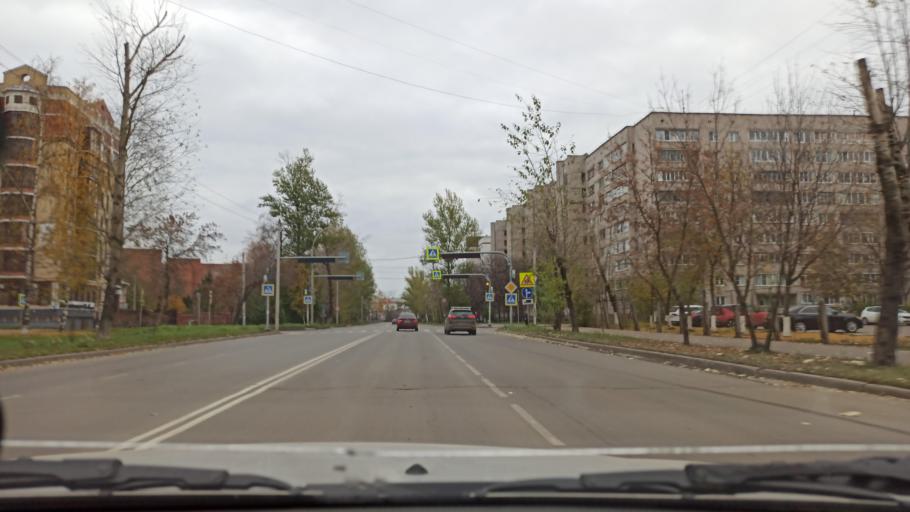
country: RU
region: Vologda
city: Vologda
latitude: 59.2150
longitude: 39.8768
